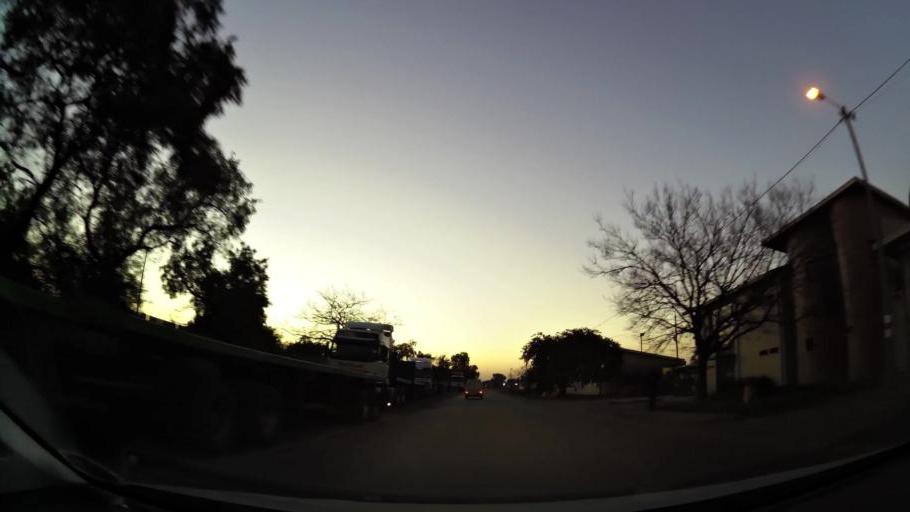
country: ZA
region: North-West
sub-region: Bojanala Platinum District Municipality
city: Rustenburg
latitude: -25.6771
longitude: 27.2561
